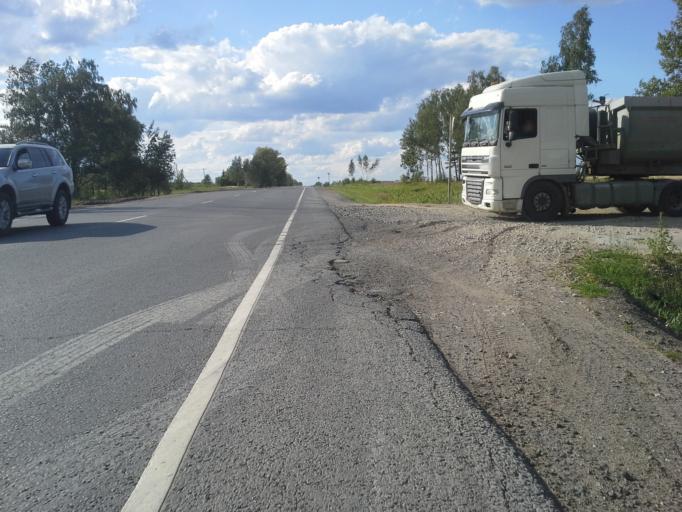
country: RU
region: Moskovskaya
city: Klimovsk
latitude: 55.3547
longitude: 37.4410
